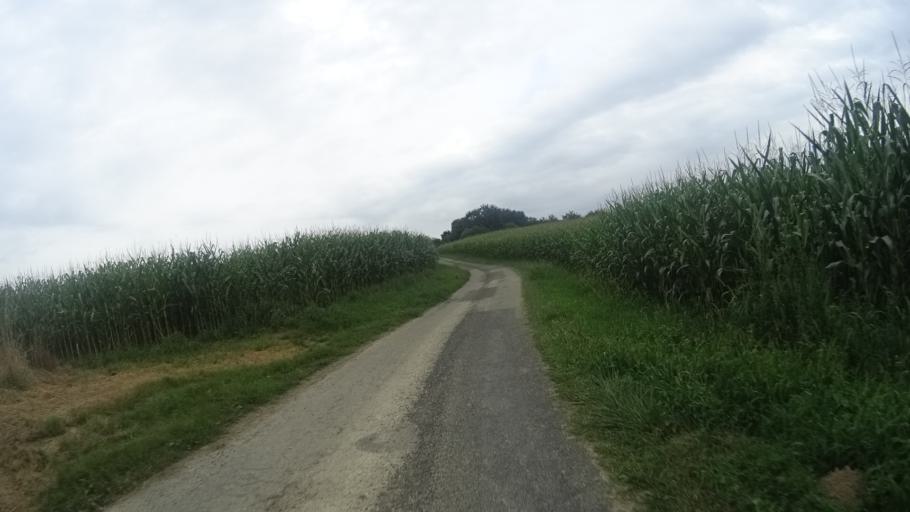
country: FR
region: Aquitaine
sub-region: Departement des Pyrenees-Atlantiques
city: Mont
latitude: 43.4987
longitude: -0.6911
